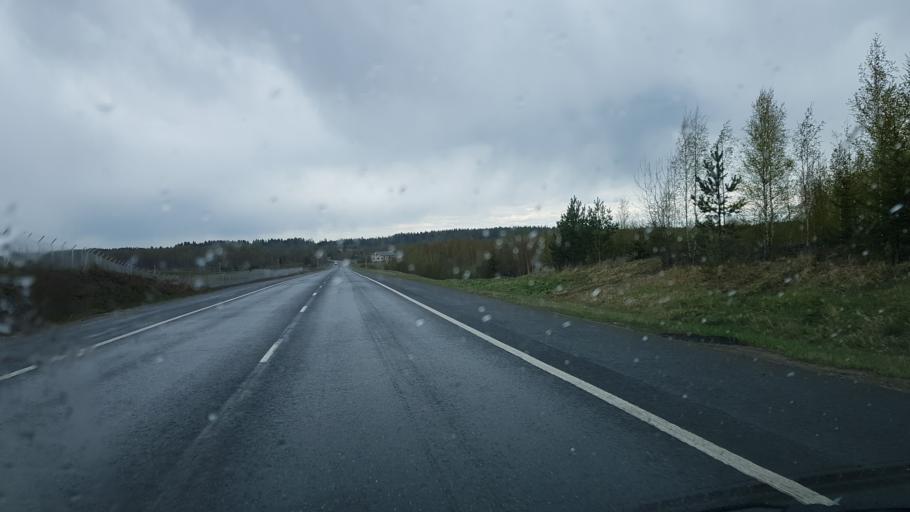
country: FI
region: Pirkanmaa
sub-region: Tampere
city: Pirkkala
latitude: 61.4175
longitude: 23.6344
